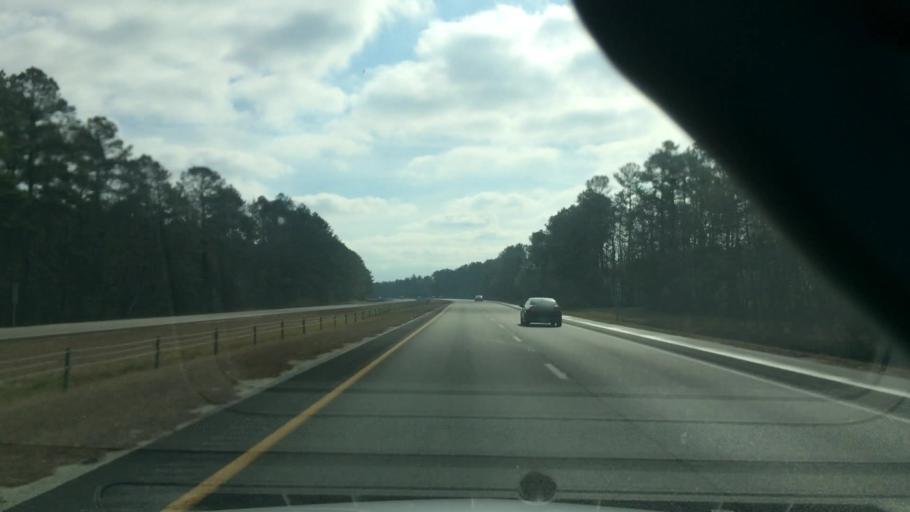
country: US
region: North Carolina
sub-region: Pender County
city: Burgaw
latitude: 34.5397
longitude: -77.8935
